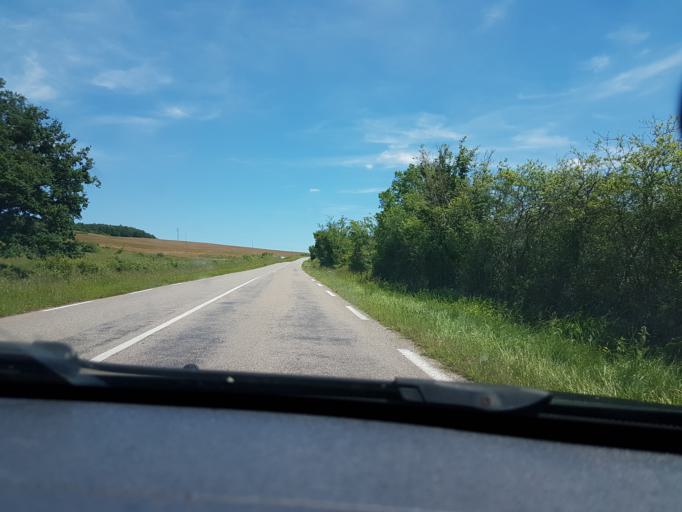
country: FR
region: Bourgogne
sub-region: Departement de Saone-et-Loire
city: Epinac
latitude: 46.9729
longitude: 4.5074
